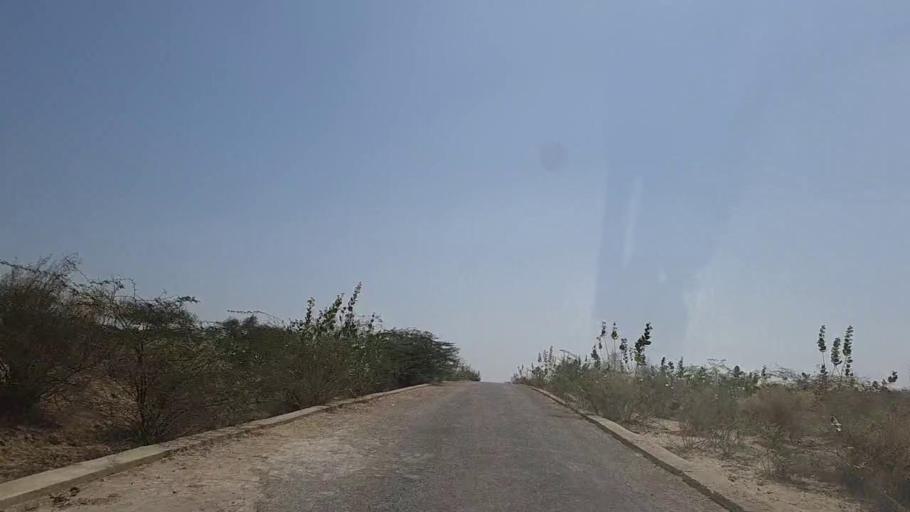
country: PK
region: Sindh
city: Diplo
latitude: 24.5053
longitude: 69.4253
